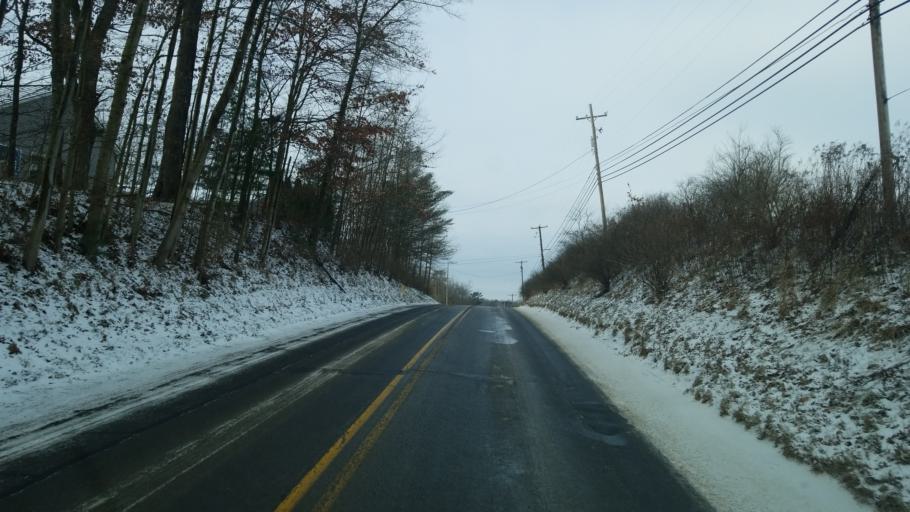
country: US
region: Pennsylvania
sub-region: Clarion County
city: Knox
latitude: 41.2344
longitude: -79.5620
